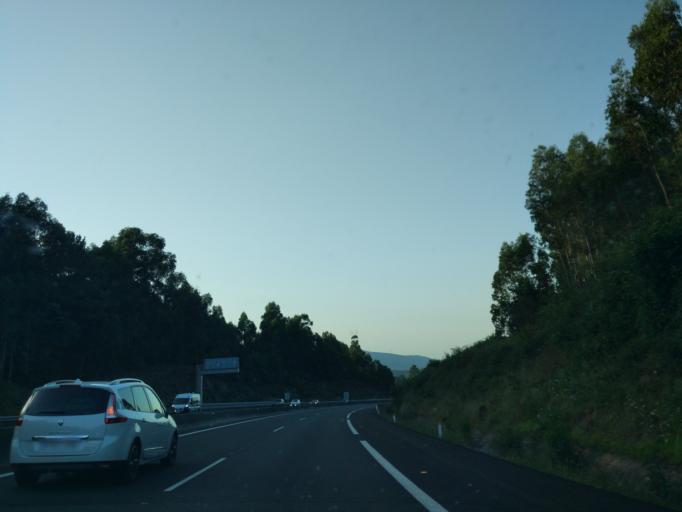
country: ES
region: Galicia
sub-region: Provincia de Pontevedra
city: Barro
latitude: 42.5263
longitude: -8.6701
